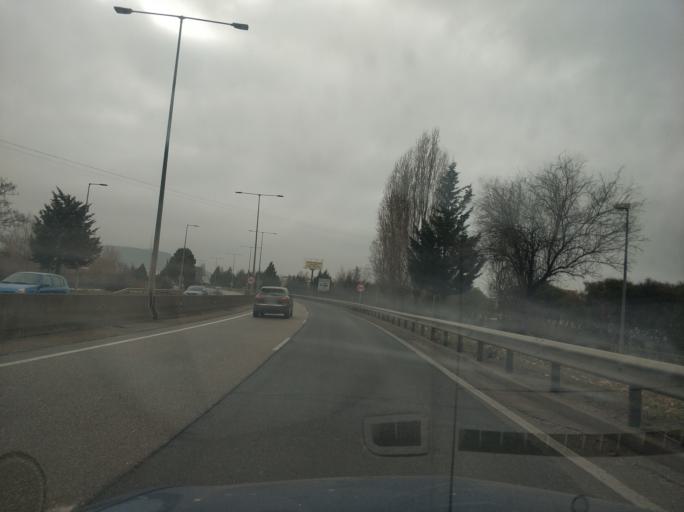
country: ES
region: Castille and Leon
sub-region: Provincia de Valladolid
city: Valladolid
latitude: 41.6408
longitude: -4.7027
